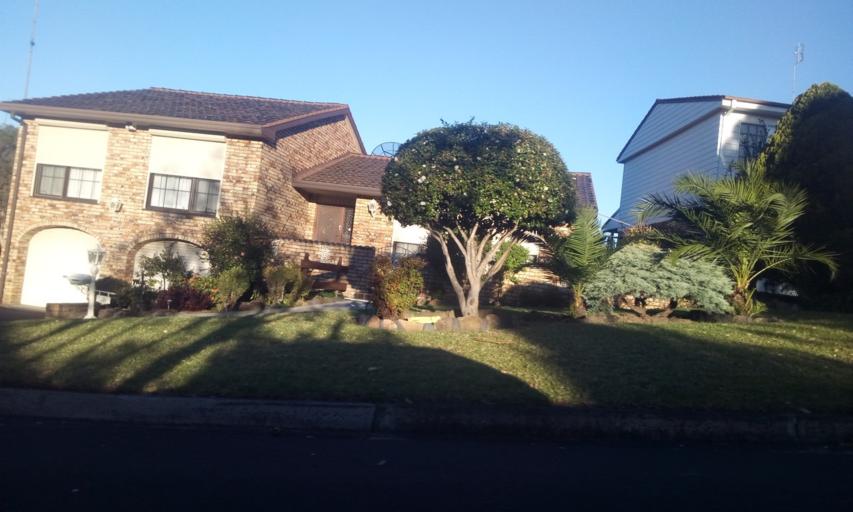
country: AU
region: New South Wales
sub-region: Wollongong
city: Mount Keira
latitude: -34.4213
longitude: 150.8545
